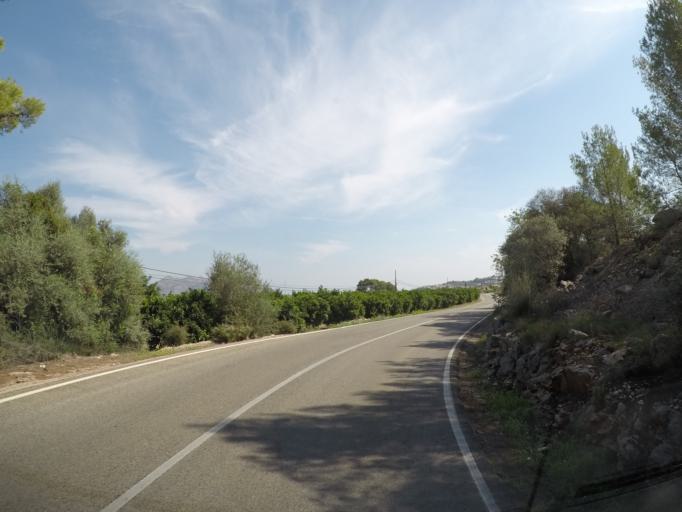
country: ES
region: Valencia
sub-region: Provincia de Alicante
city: Orba
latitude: 38.7810
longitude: -0.0772
